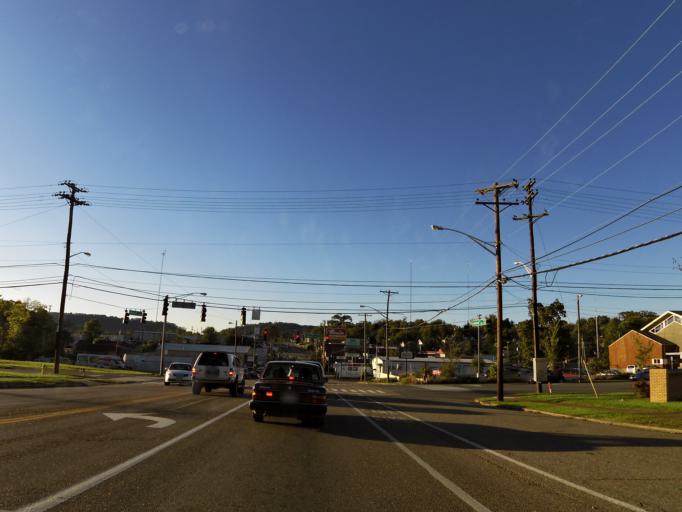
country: US
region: Tennessee
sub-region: Knox County
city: Knoxville
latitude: 35.9805
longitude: -83.9282
